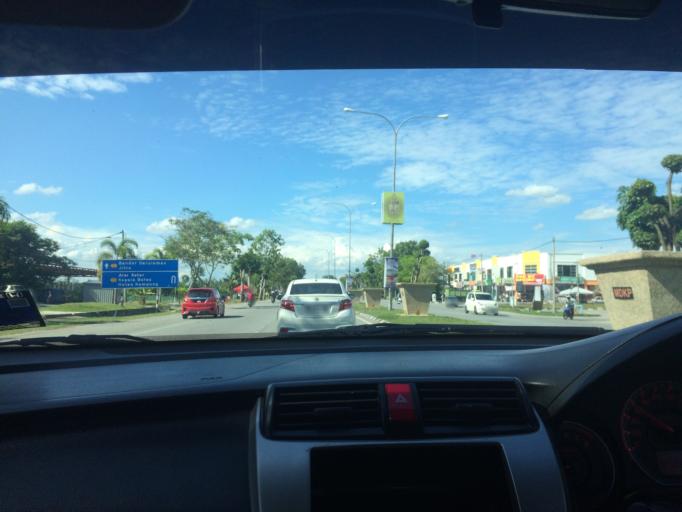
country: MY
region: Kedah
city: Jitra
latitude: 6.2065
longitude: 100.4137
